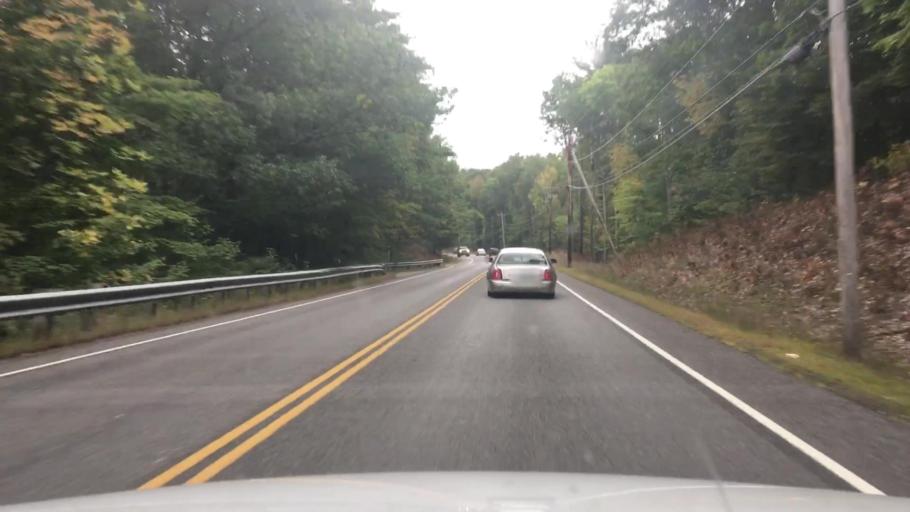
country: US
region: New Hampshire
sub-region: Strafford County
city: New Durham
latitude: 43.4913
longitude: -71.2546
